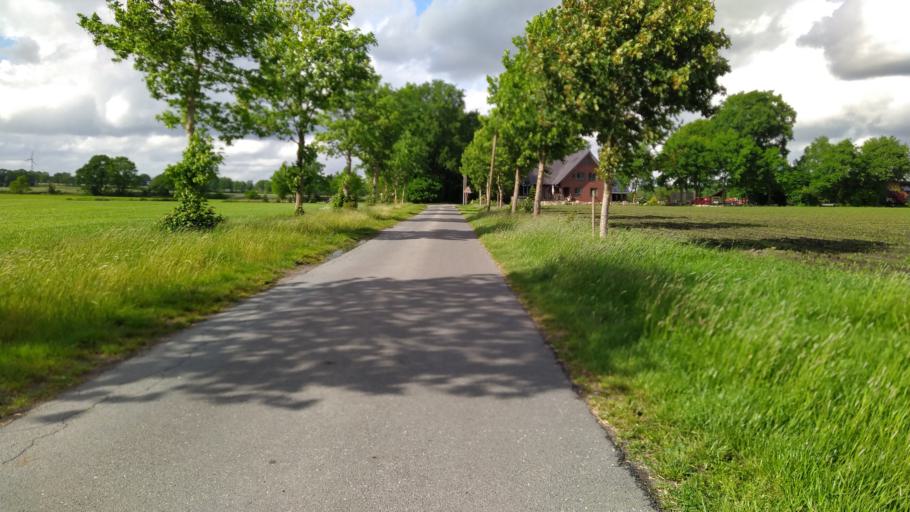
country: DE
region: Lower Saxony
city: Brest
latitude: 53.4571
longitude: 9.3923
